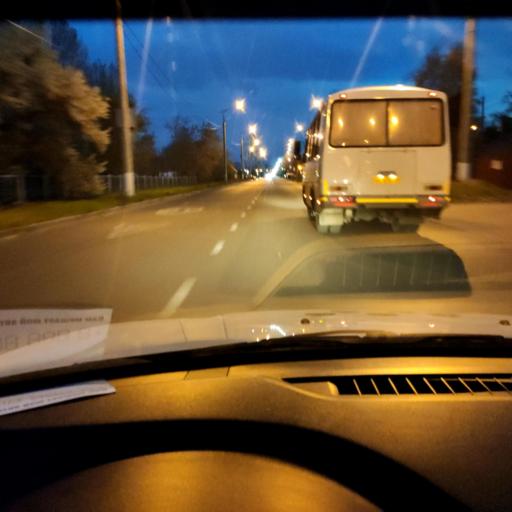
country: RU
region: Samara
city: Tol'yatti
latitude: 53.5116
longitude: 49.3953
